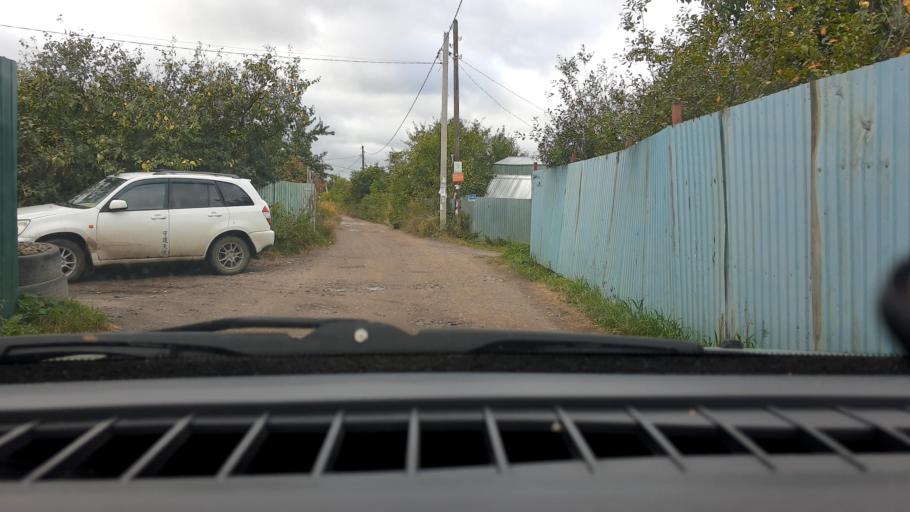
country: RU
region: Nizjnij Novgorod
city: Gorbatovka
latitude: 56.3204
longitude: 43.8377
